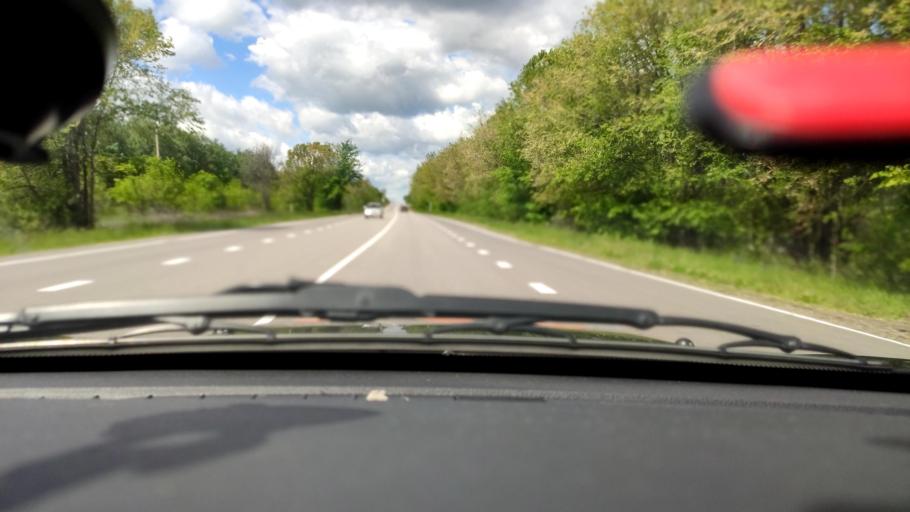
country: RU
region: Belgorod
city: Krasnoye
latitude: 51.0678
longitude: 38.8093
